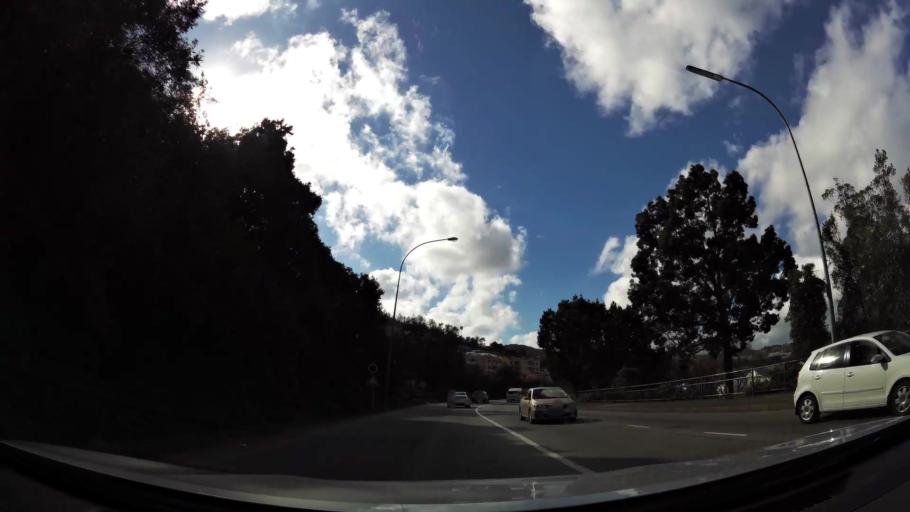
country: ZA
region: Western Cape
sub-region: Eden District Municipality
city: Knysna
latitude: -34.0380
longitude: 23.0635
